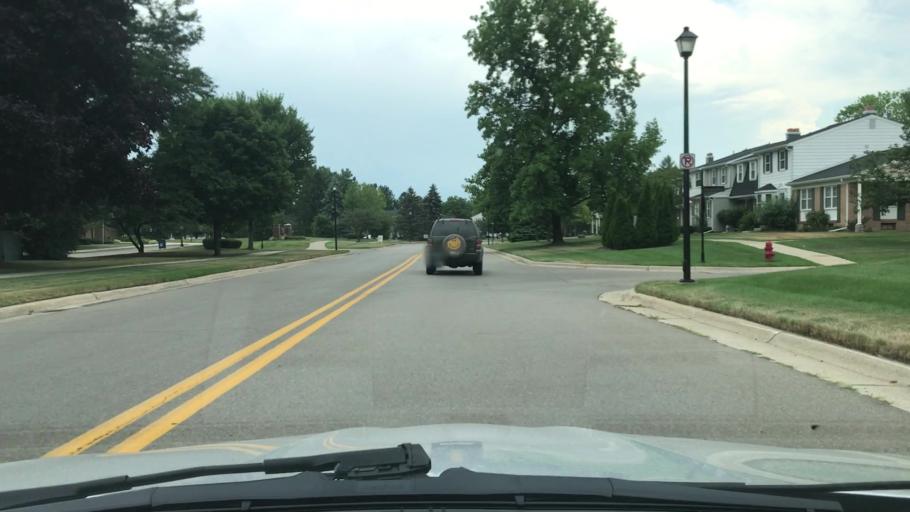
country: US
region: Michigan
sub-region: Wayne County
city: Northville
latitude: 42.4341
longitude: -83.4651
